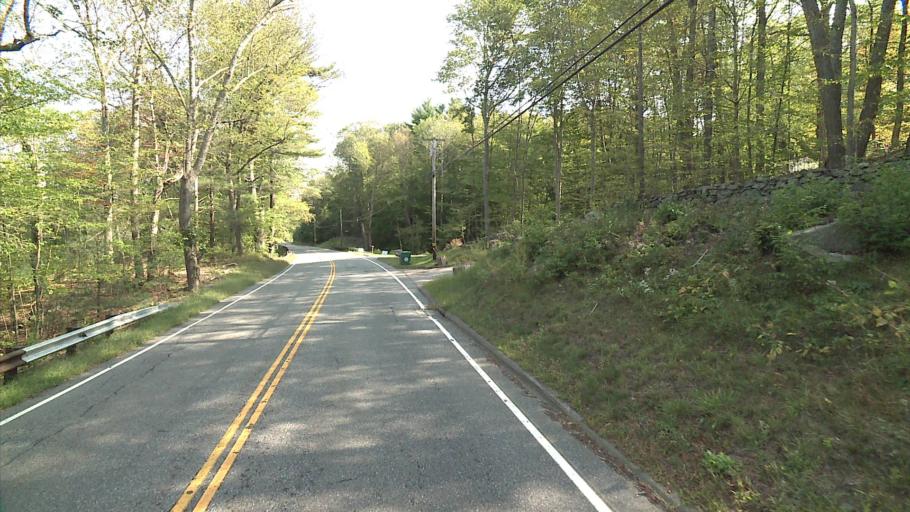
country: US
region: Connecticut
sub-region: New London County
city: Jewett City
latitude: 41.6359
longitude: -71.9957
